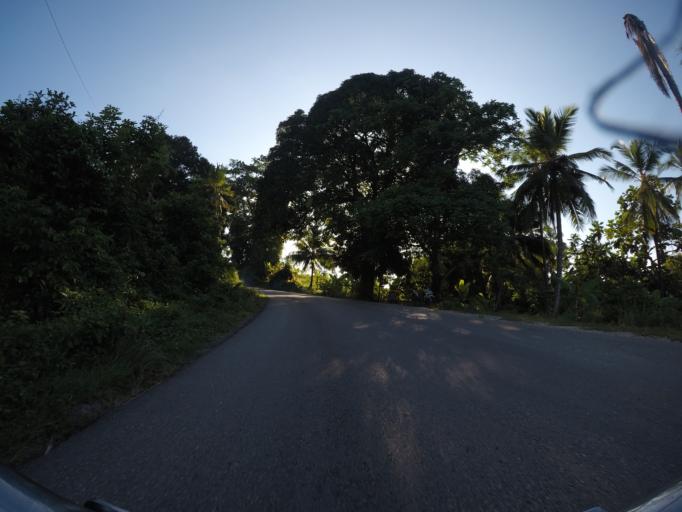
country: TZ
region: Pemba South
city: Chake Chake
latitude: -5.3056
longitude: 39.7500
